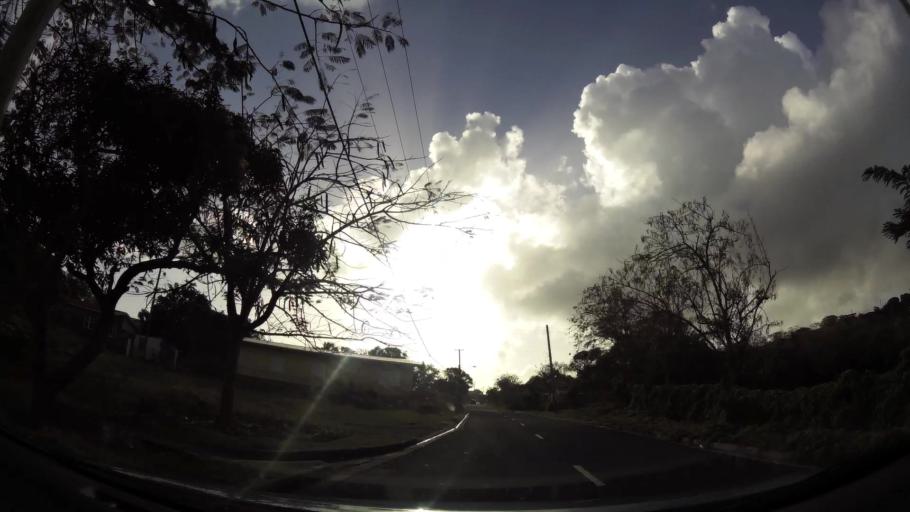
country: KN
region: Saint George Gingerland
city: Market Shop
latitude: 17.1313
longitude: -62.5779
